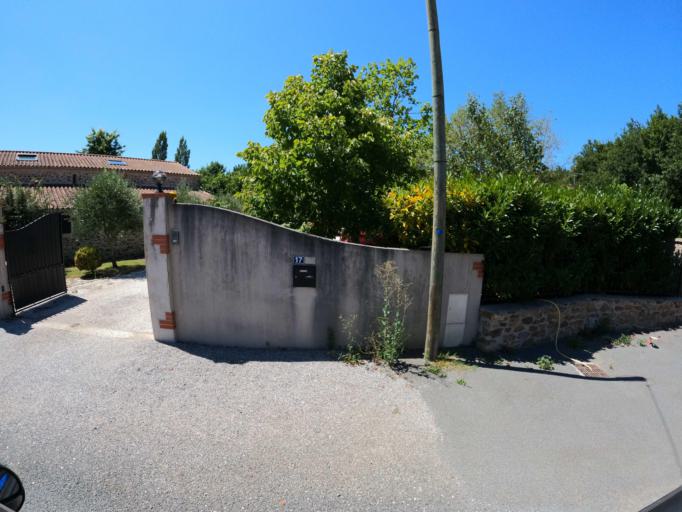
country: FR
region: Pays de la Loire
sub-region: Departement de la Loire-Atlantique
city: La Limouziniere
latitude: 46.9406
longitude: -1.6226
